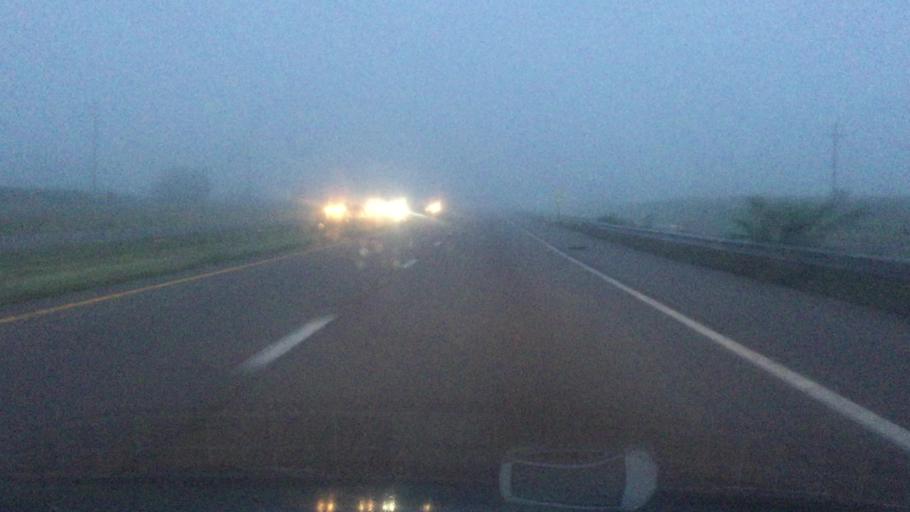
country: US
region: Missouri
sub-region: Montgomery County
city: Montgomery City
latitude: 38.8863
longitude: -91.4091
